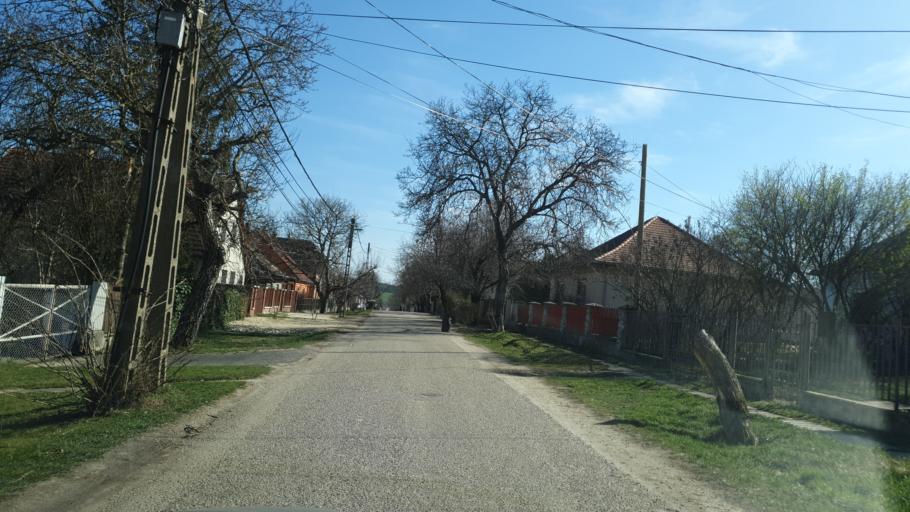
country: HU
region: Fejer
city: Etyek
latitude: 47.4544
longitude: 18.7542
